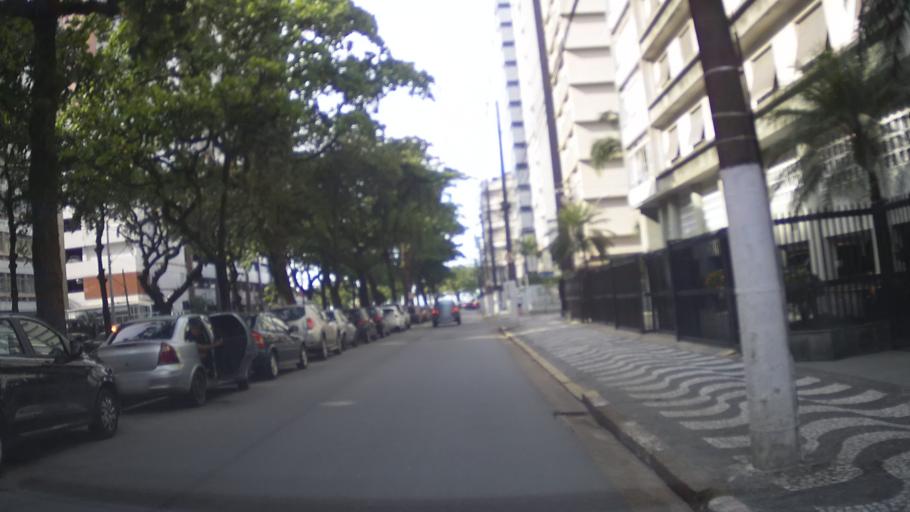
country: BR
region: Sao Paulo
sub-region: Santos
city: Santos
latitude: -23.9689
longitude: -46.3292
